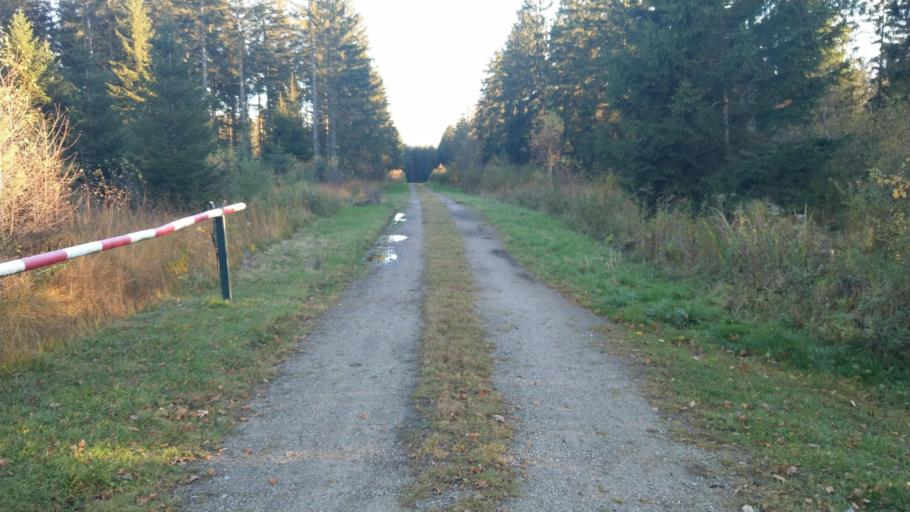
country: BE
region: Wallonia
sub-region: Province de Liege
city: Raeren
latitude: 50.6453
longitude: 6.1463
